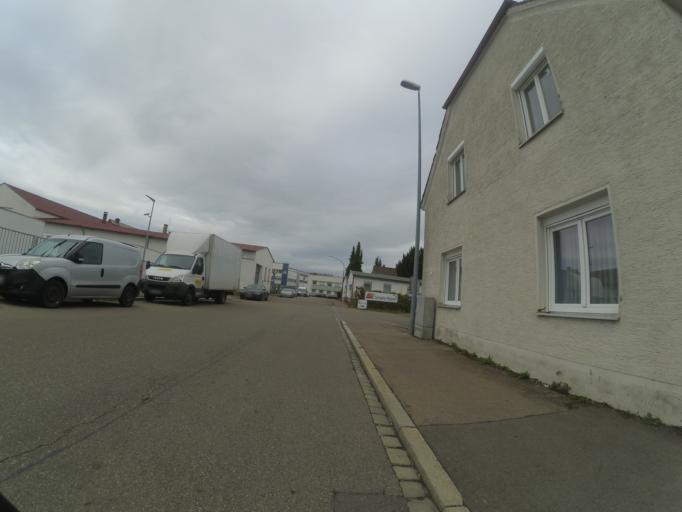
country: DE
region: Bavaria
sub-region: Swabia
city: Neu-Ulm
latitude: 48.3966
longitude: 10.0148
